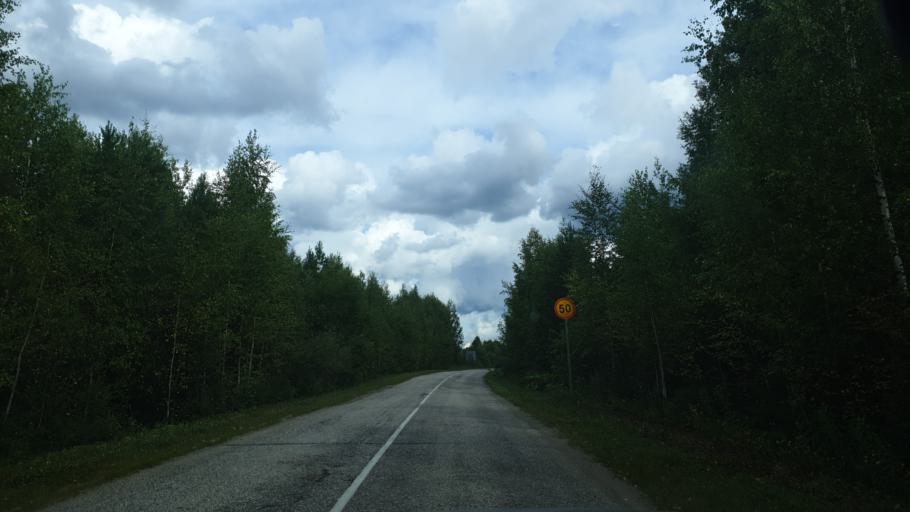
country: RU
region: Komi Republic
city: Aykino
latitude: 61.9356
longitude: 50.1559
